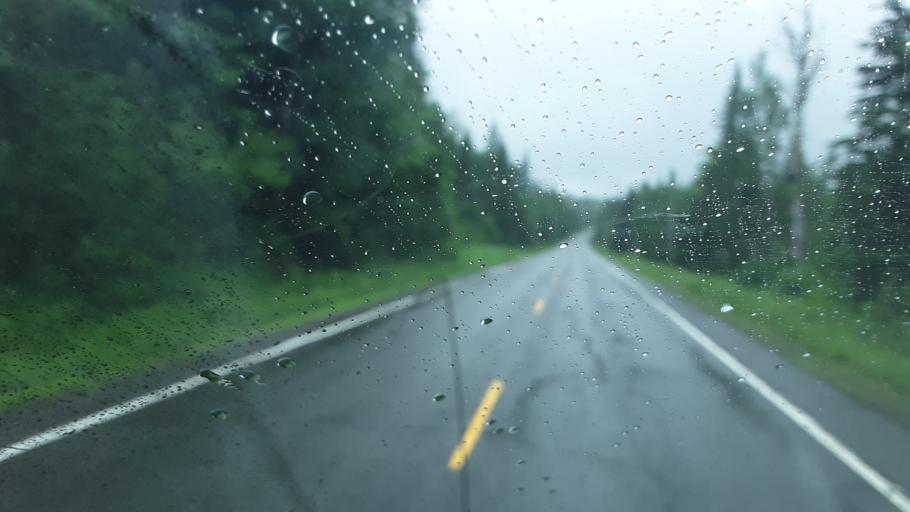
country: US
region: Maine
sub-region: Penobscot County
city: Patten
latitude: 46.1916
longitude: -68.3337
